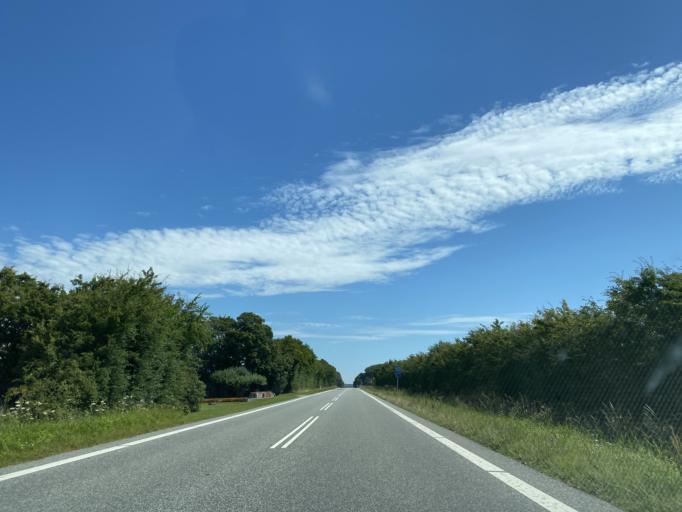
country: DK
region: South Denmark
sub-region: Faaborg-Midtfyn Kommune
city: Faaborg
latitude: 55.1091
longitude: 10.1802
